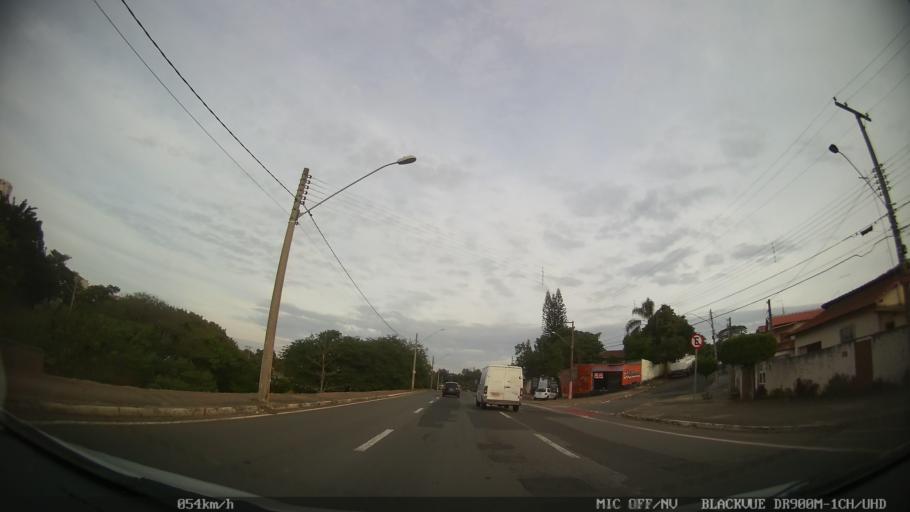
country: BR
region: Sao Paulo
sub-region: Limeira
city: Limeira
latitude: -22.5814
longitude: -47.4119
